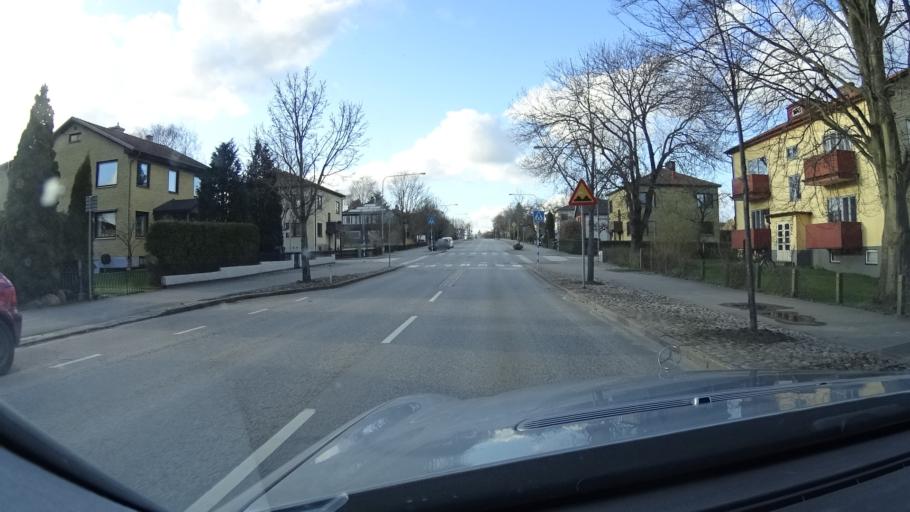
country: SE
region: Skane
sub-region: Hoors Kommun
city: Hoeoer
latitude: 55.9281
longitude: 13.5438
